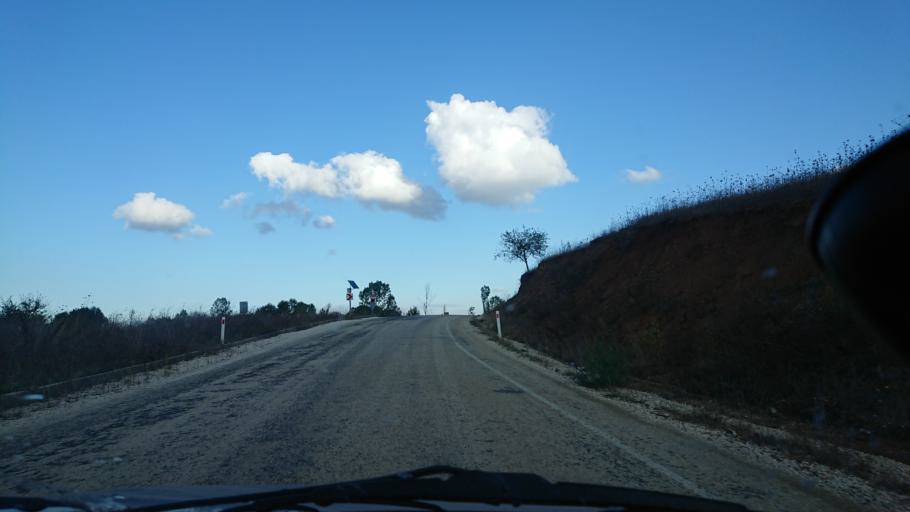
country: TR
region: Bilecik
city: Pazaryeri
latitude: 40.0116
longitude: 29.8567
